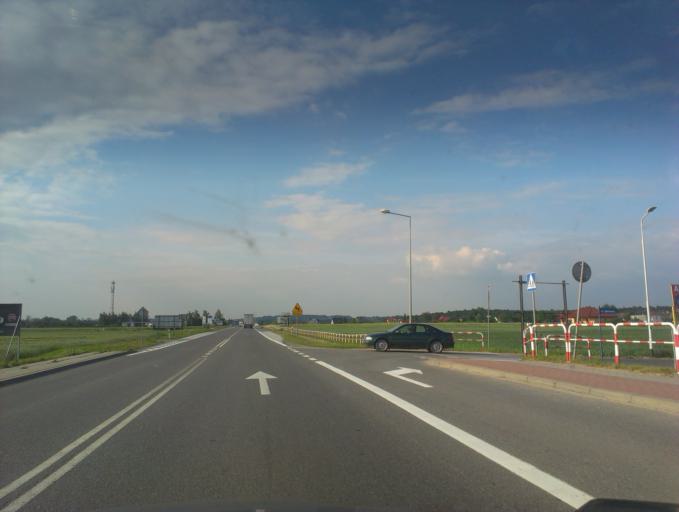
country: PL
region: Lower Silesian Voivodeship
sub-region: Powiat trzebnicki
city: Psary
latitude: 51.2341
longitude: 17.0432
